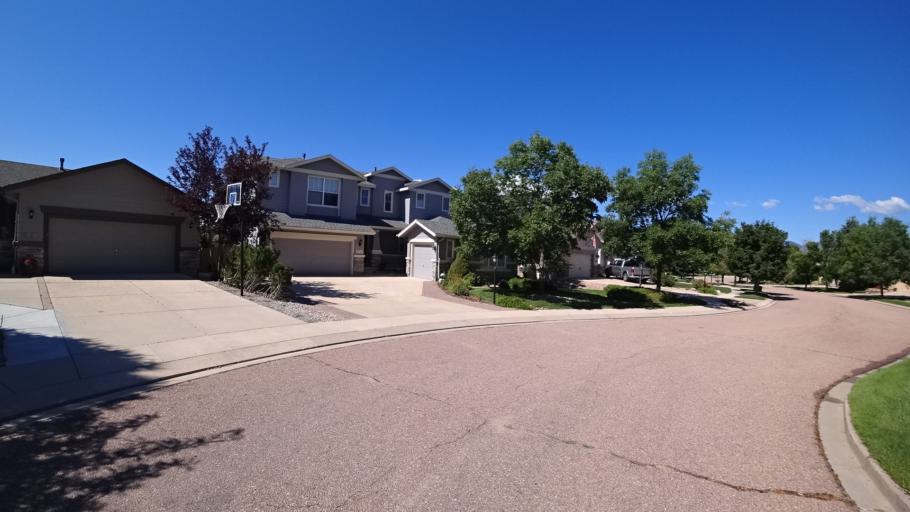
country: US
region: Colorado
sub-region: El Paso County
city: Gleneagle
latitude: 38.9750
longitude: -104.7774
